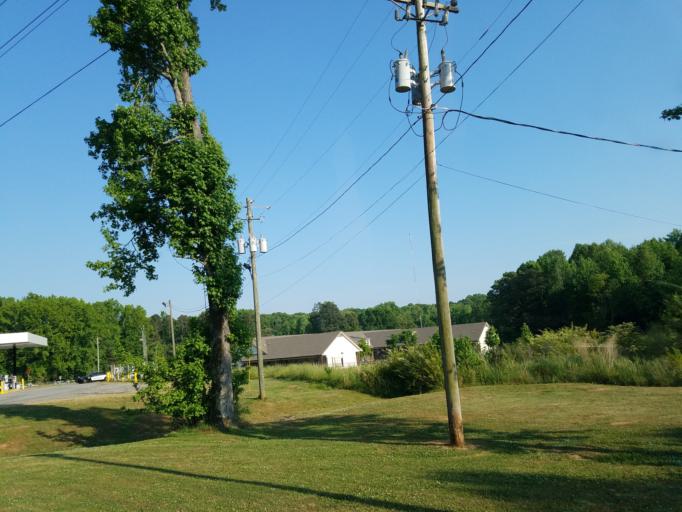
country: US
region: Georgia
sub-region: Forsyth County
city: Cumming
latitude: 34.2707
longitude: -84.0860
